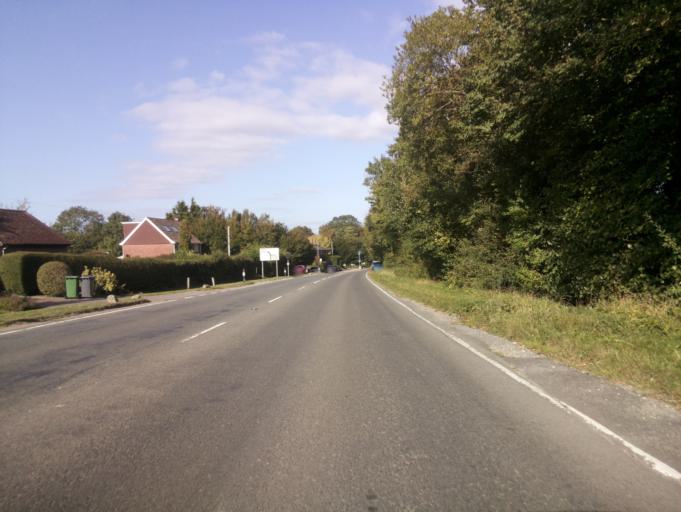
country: GB
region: England
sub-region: Hampshire
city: Basingstoke
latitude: 51.2953
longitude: -1.1150
